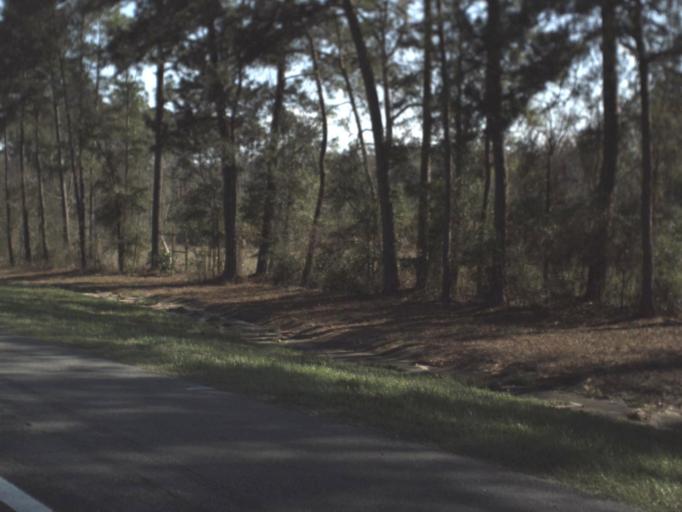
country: US
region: Florida
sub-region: Gadsden County
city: Midway
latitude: 30.5040
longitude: -84.4593
